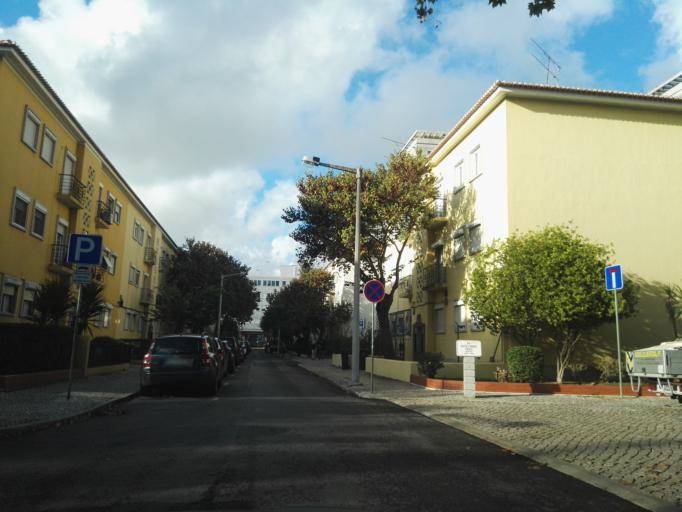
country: PT
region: Lisbon
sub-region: Lisbon
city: Lisbon
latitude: 38.7512
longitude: -9.1448
